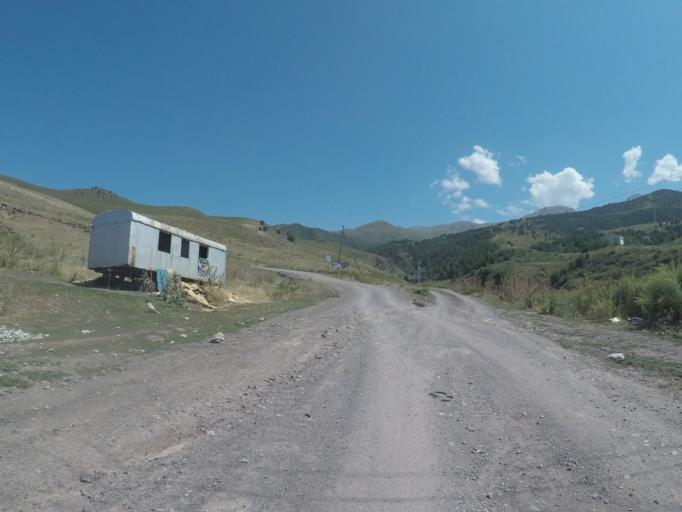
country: KG
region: Chuy
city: Bishkek
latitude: 42.6474
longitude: 74.5136
